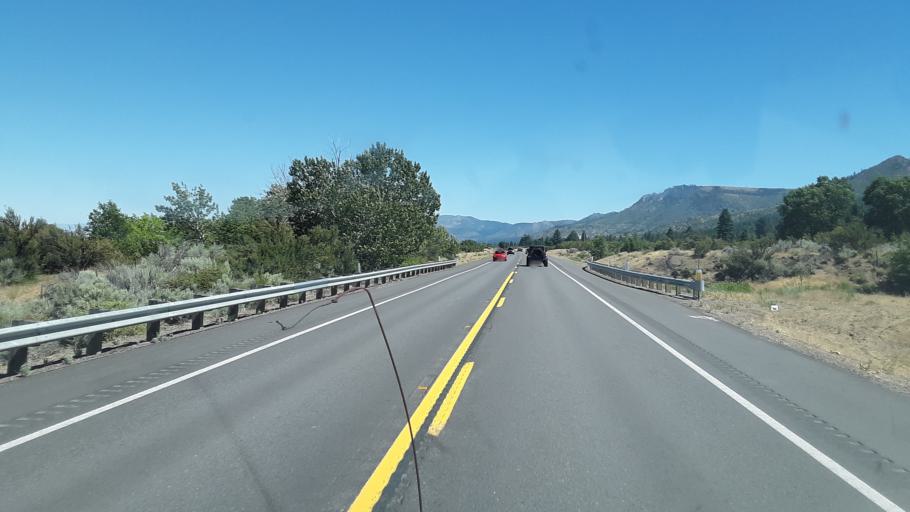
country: US
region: California
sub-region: Lassen County
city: Janesville
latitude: 40.2758
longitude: -120.4834
